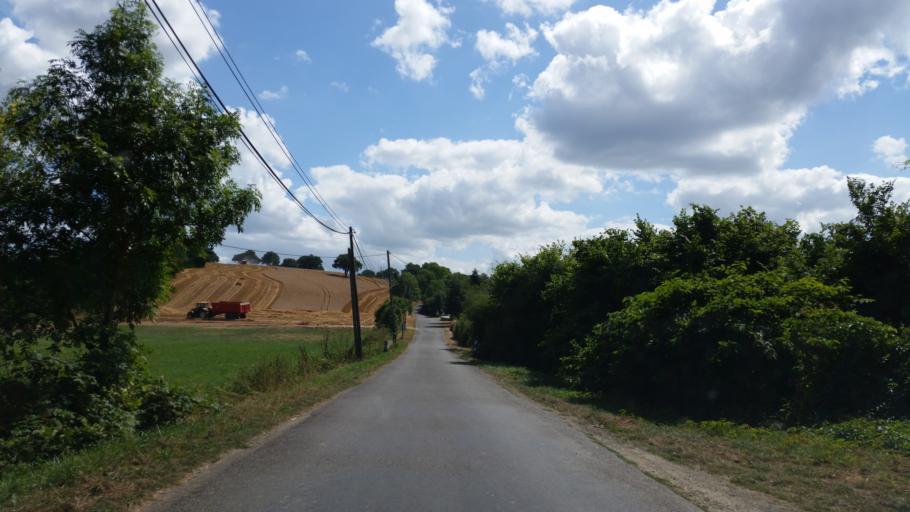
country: FR
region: Lower Normandy
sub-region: Departement du Calvados
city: Clecy
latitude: 48.8493
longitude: -0.3822
